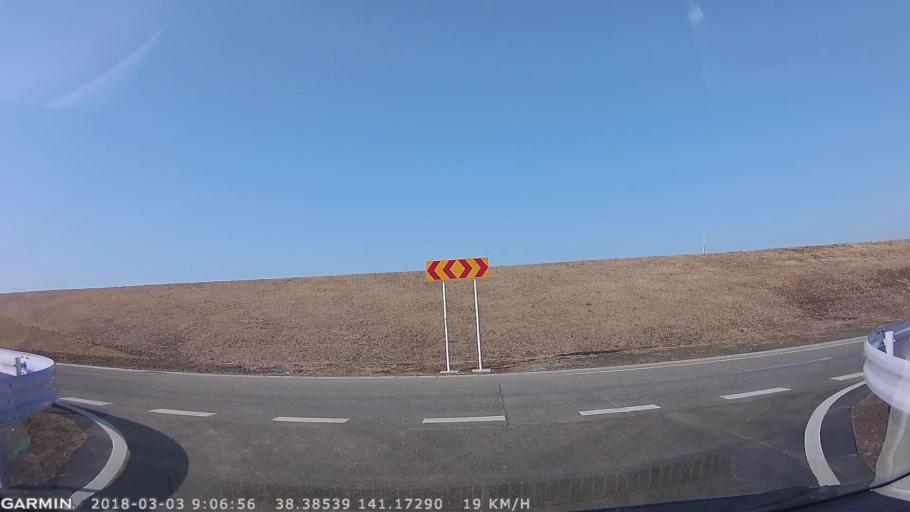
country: JP
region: Miyagi
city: Yamoto
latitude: 38.3854
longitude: 141.1729
